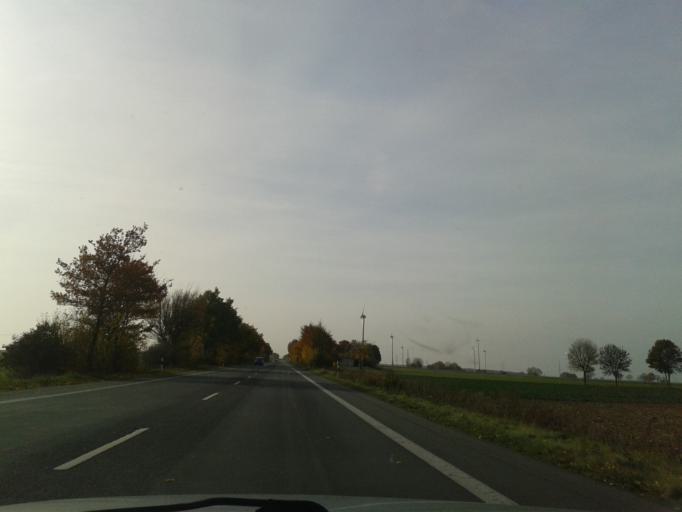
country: DE
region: North Rhine-Westphalia
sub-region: Regierungsbezirk Detmold
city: Buren
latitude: 51.5744
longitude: 8.5501
